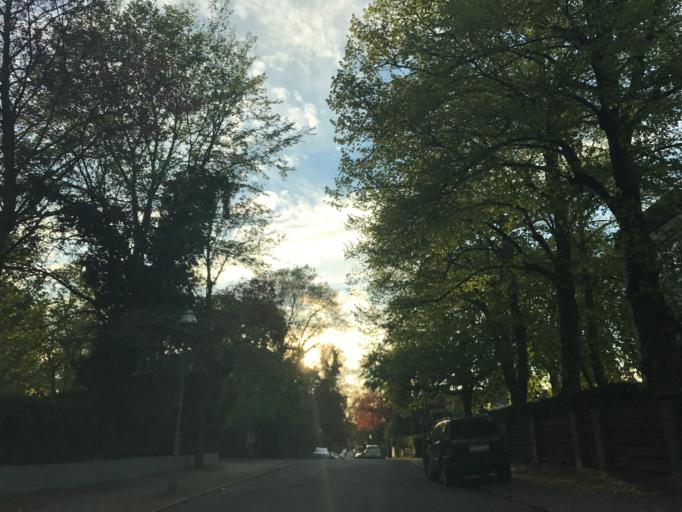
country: DE
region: Berlin
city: Westend
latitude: 52.5143
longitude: 13.2709
